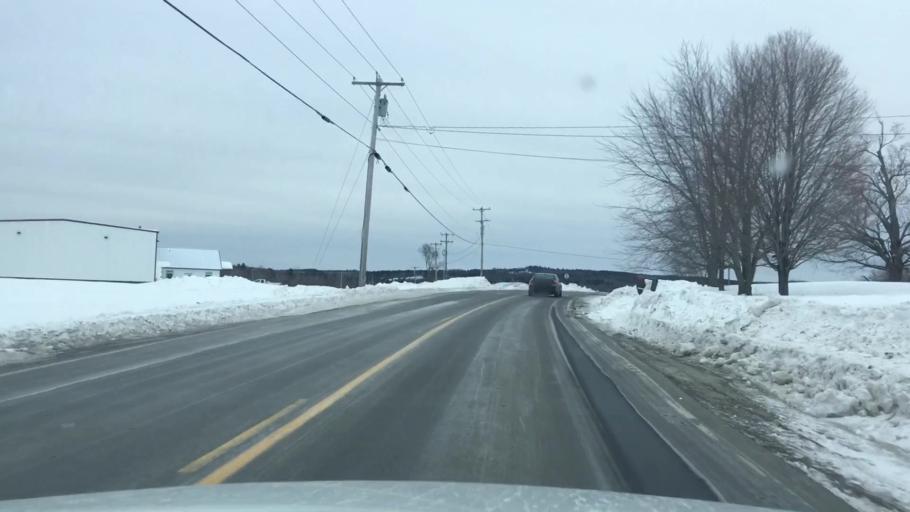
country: US
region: Maine
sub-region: Penobscot County
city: Garland
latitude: 44.9776
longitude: -69.0901
